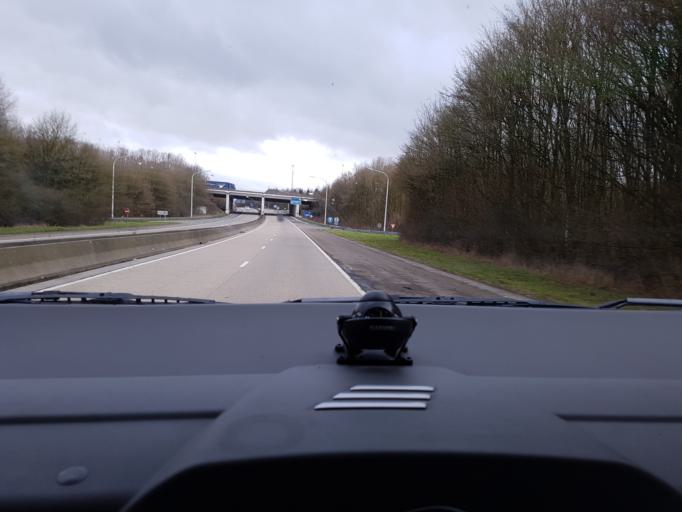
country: BE
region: Wallonia
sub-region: Province de Namur
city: Ciney
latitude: 50.2691
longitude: 5.0383
